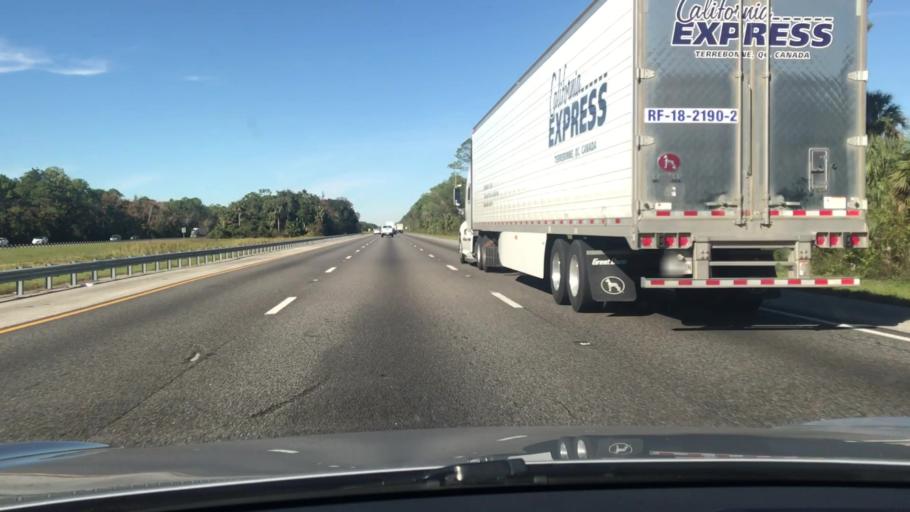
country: US
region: Florida
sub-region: Flagler County
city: Flagler Beach
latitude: 29.4264
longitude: -81.1648
